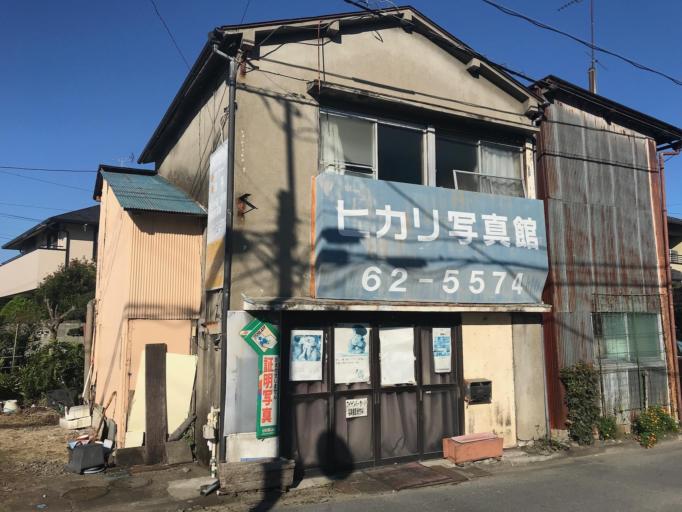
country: JP
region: Tochigi
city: Kanuma
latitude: 36.5707
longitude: 139.7484
